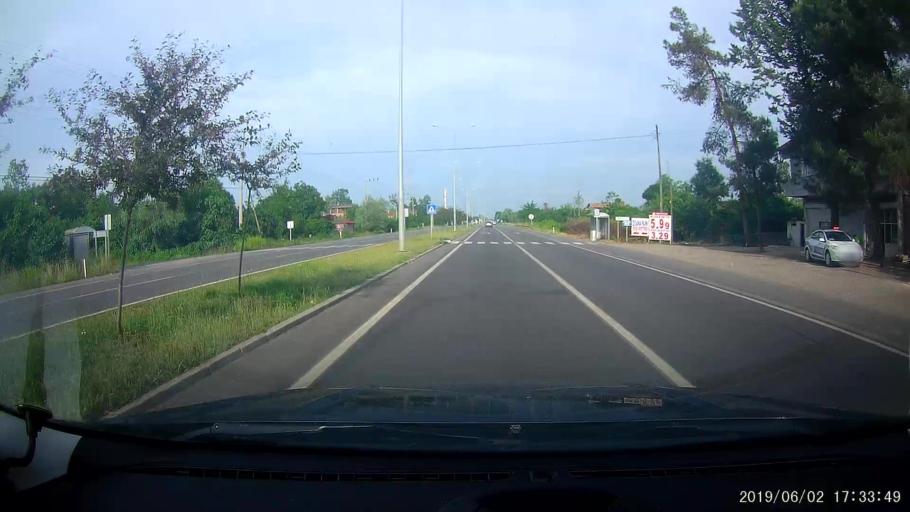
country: TR
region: Samsun
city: Terme
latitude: 41.2207
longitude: 36.8567
